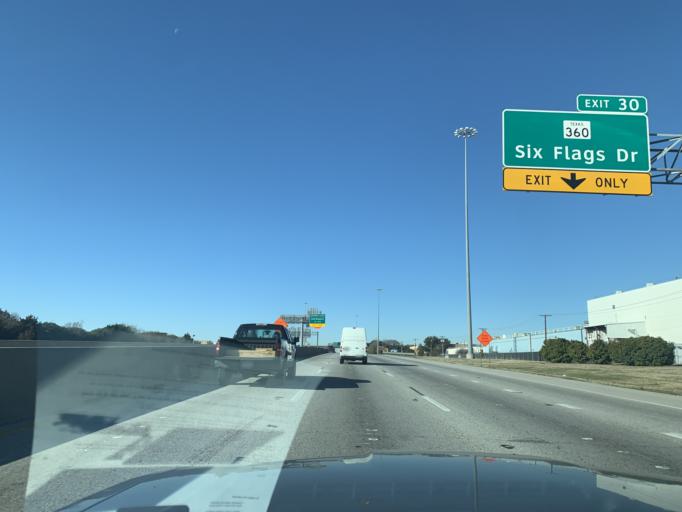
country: US
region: Texas
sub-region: Dallas County
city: Grand Prairie
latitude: 32.7602
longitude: -97.0401
